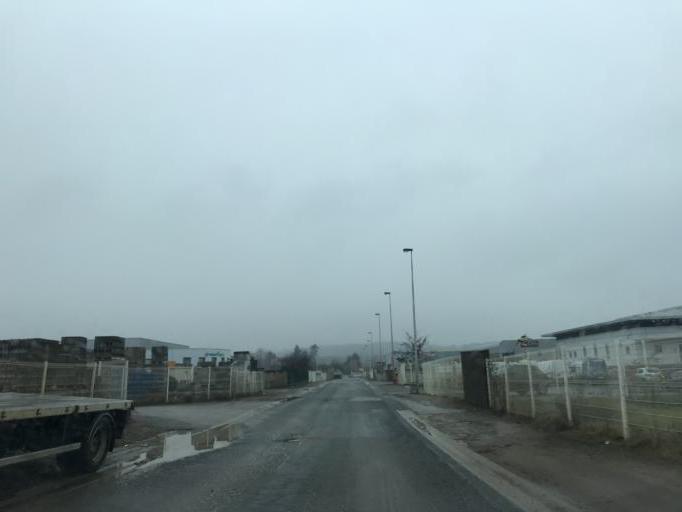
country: FR
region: Rhone-Alpes
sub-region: Departement de l'Ain
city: Jassans-Riottier
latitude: 45.9784
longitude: 4.7440
